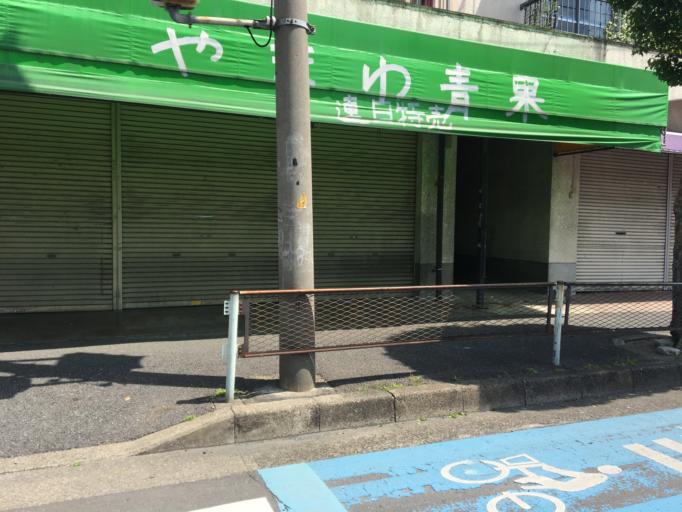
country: JP
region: Saitama
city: Iwatsuki
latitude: 35.9666
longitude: 139.7080
